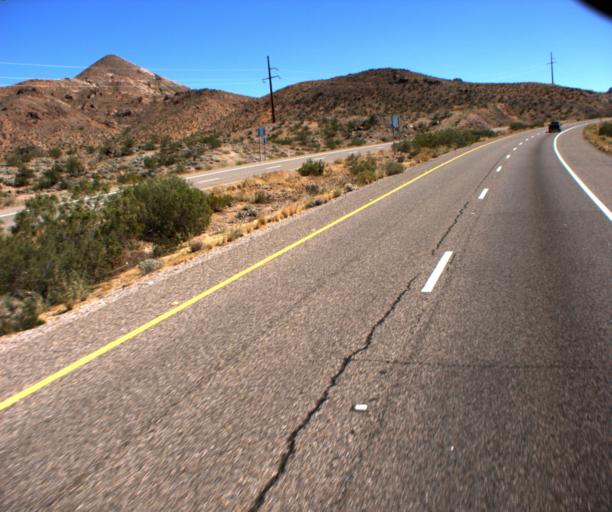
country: US
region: Nevada
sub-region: Clark County
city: Laughlin
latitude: 35.1938
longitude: -114.4398
